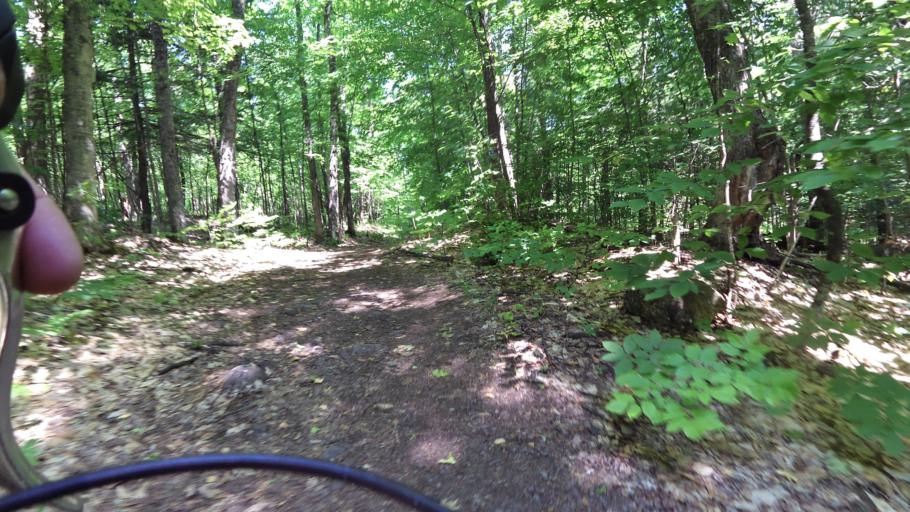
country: CA
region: Quebec
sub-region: Outaouais
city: Wakefield
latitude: 45.5449
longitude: -75.8925
